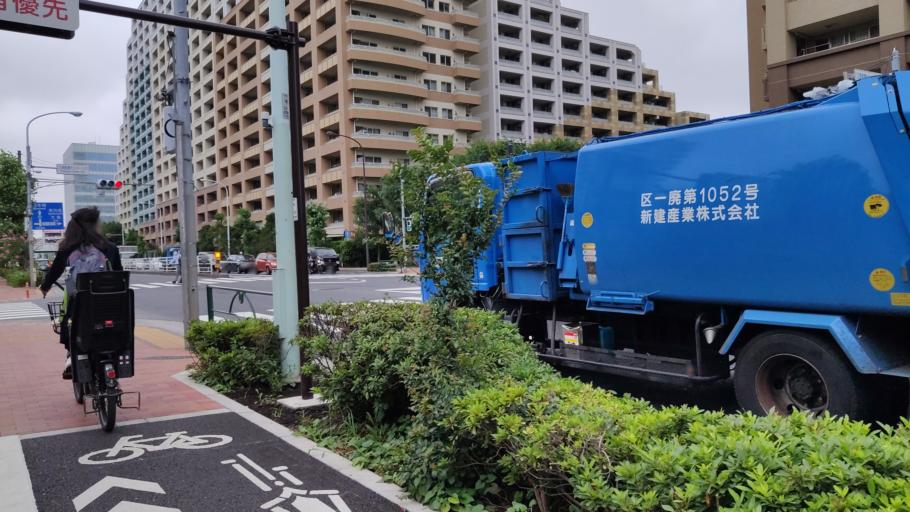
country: JP
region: Tokyo
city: Urayasu
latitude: 35.6662
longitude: 139.8349
